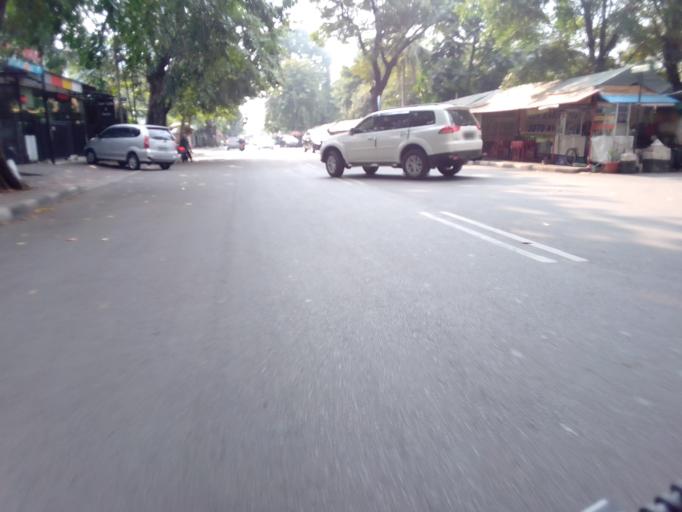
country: ID
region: Jakarta Raya
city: Jakarta
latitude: -6.2048
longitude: 106.8060
